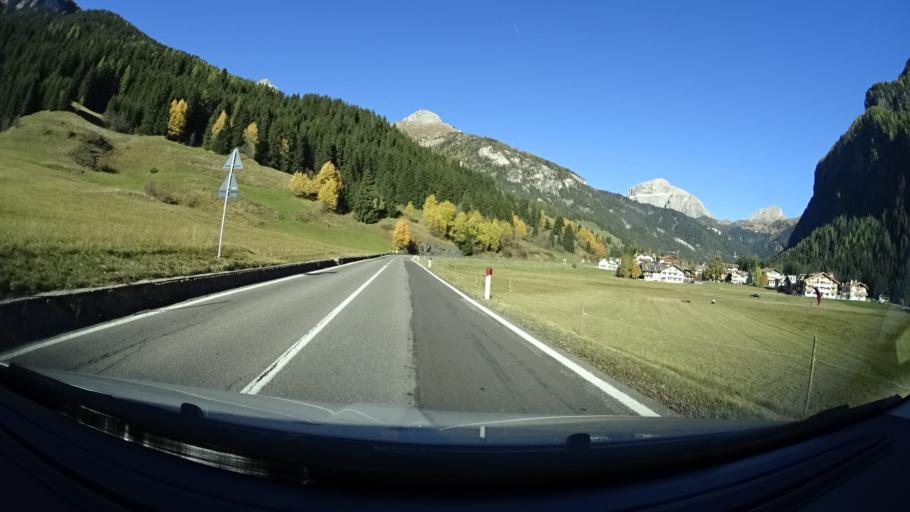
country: IT
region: Trentino-Alto Adige
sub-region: Provincia di Trento
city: Campitello di Fassa
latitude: 46.4712
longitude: 11.7302
